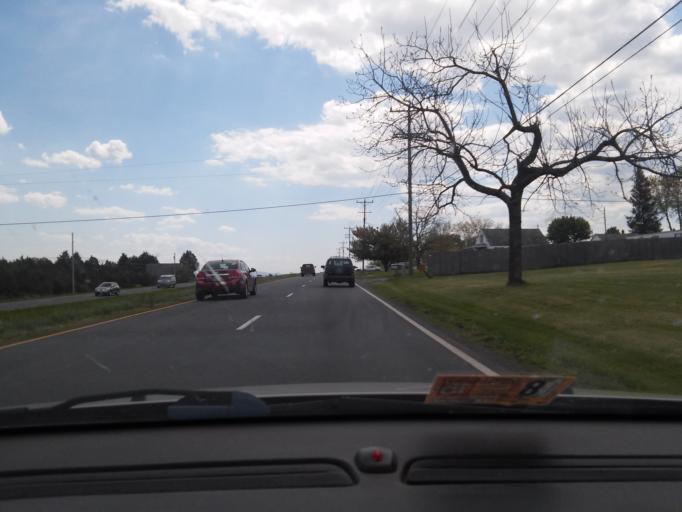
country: US
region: Virginia
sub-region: Frederick County
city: Stephens City
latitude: 39.0322
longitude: -78.1543
